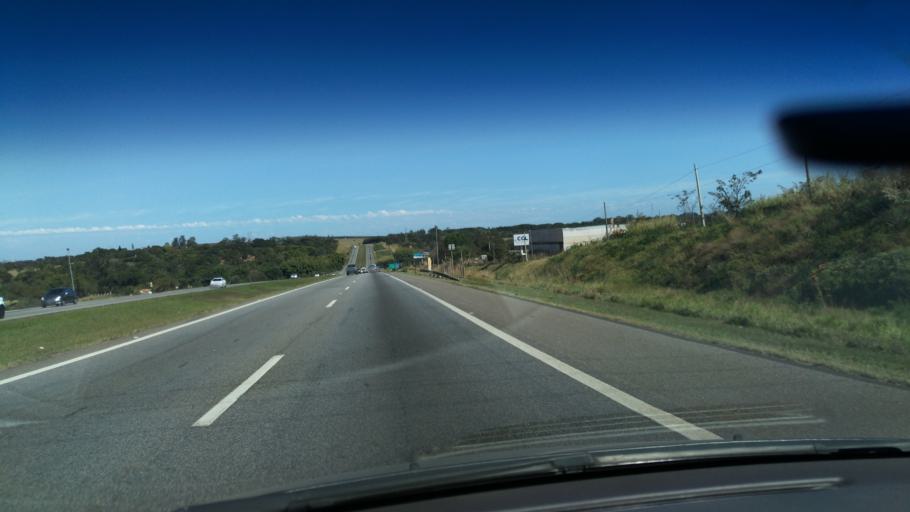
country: BR
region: Sao Paulo
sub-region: Jaguariuna
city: Jaguariuna
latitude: -22.7301
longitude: -47.0153
